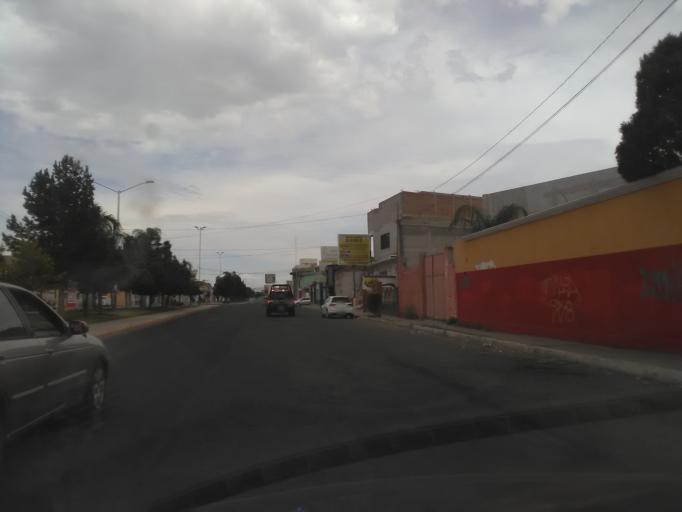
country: MX
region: Durango
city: Victoria de Durango
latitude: 24.0166
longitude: -104.6492
